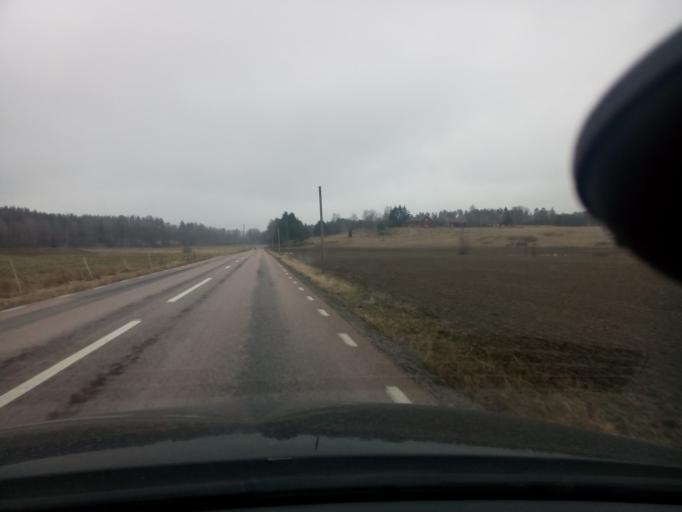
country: SE
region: Soedermanland
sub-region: Gnesta Kommun
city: Gnesta
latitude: 59.0199
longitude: 17.1696
